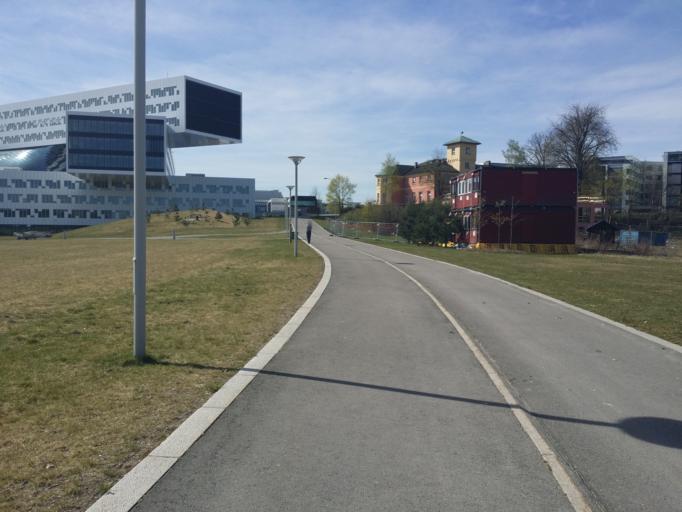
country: NO
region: Akershus
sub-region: Baerum
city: Lysaker
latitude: 59.8977
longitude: 10.6325
